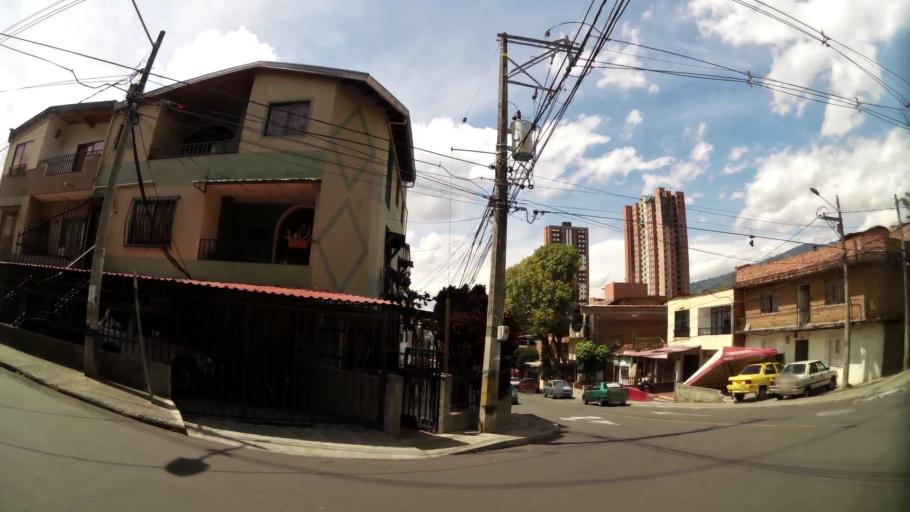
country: CO
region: Antioquia
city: Bello
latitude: 6.3441
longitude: -75.5505
